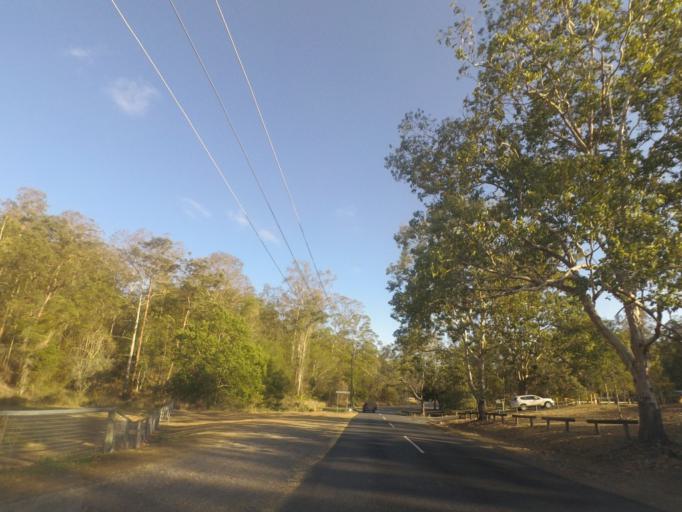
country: AU
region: Queensland
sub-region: Brisbane
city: Taringa
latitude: -27.4677
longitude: 152.9700
